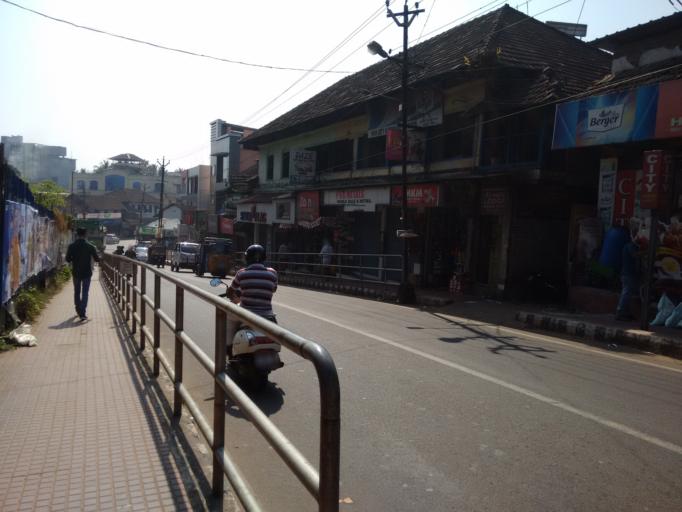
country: IN
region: Kerala
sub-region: Kozhikode
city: Badagara
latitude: 11.5961
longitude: 75.5897
